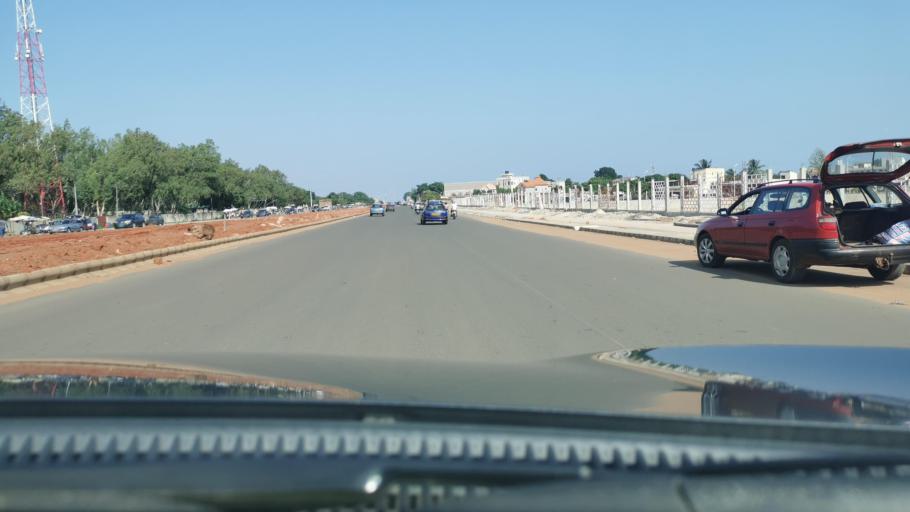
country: TG
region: Maritime
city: Lome
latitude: 6.1906
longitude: 1.1602
